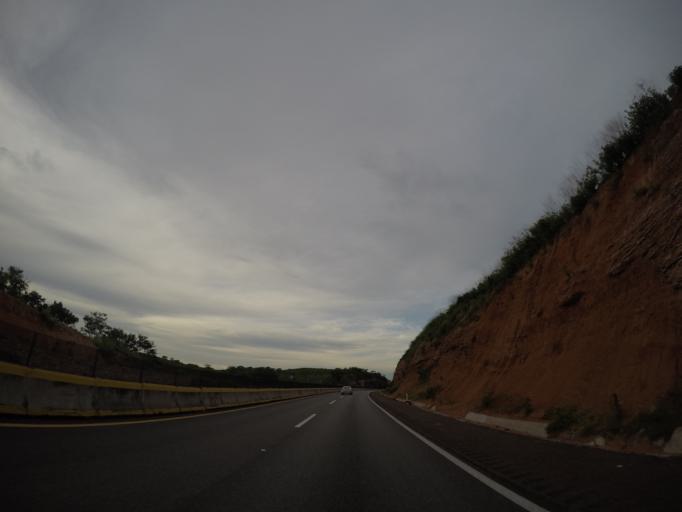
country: MX
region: Guerrero
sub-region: Huitzuco de los Figueroa
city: San Francisco Ozomatlan
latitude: 18.0633
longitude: -99.2464
